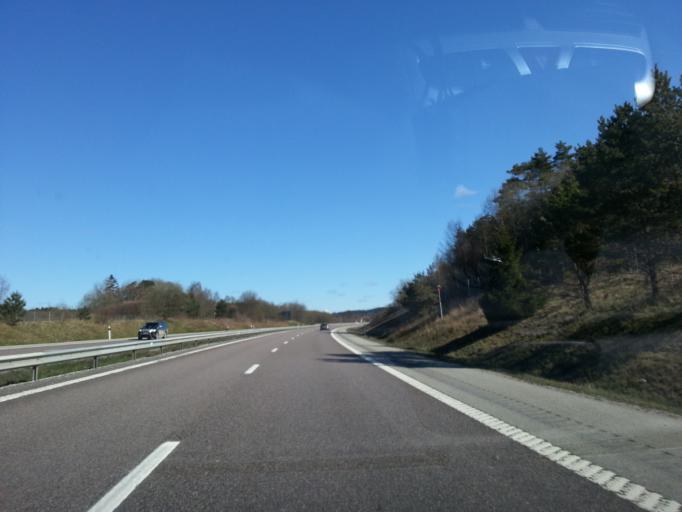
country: SE
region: Vaestra Goetaland
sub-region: Stenungsunds Kommun
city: Stora Hoga
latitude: 58.0400
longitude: 11.8465
